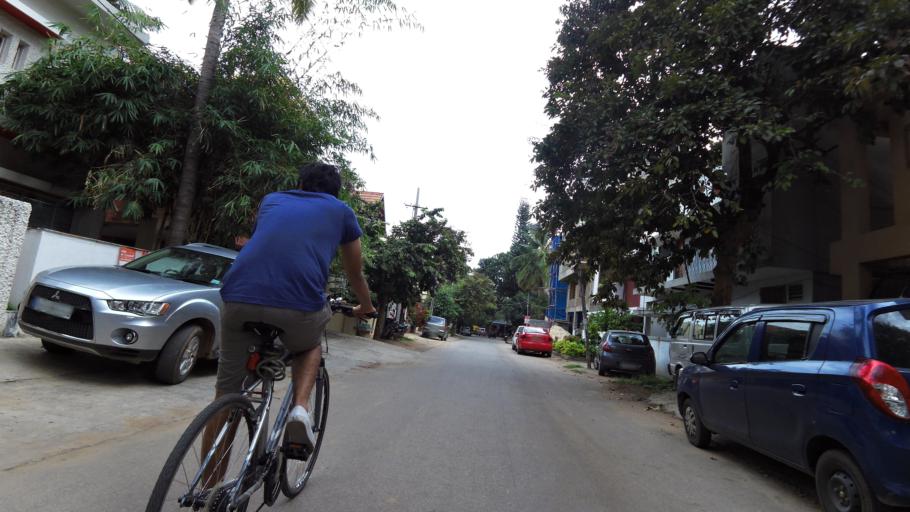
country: IN
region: Karnataka
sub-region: Bangalore Urban
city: Bangalore
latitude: 12.9692
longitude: 77.6389
